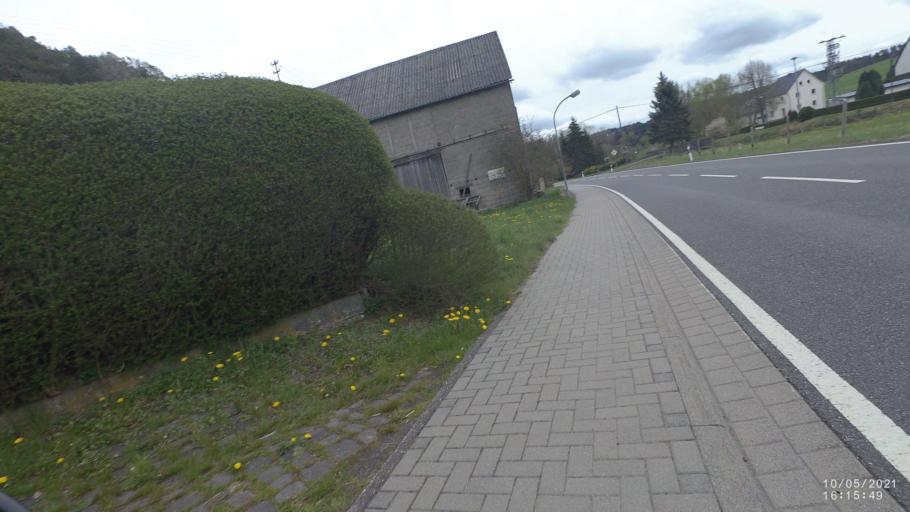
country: DE
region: Rheinland-Pfalz
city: Lind
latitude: 50.3415
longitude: 7.0452
